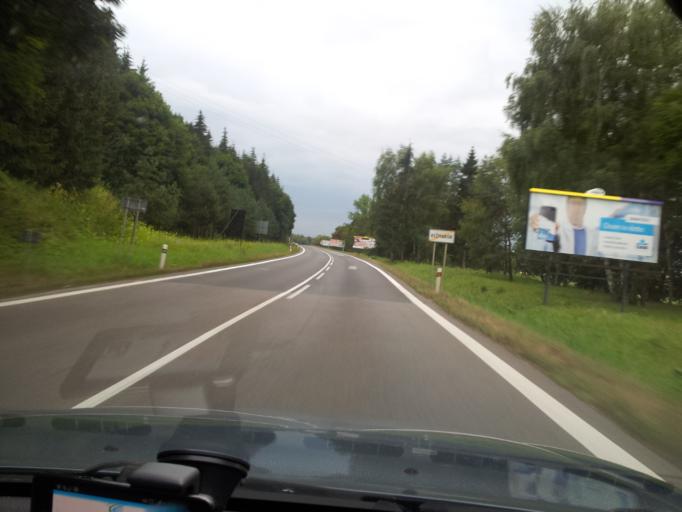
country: SK
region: Presovsky
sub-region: Okres Presov
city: Kezmarok
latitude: 49.1301
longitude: 20.4181
